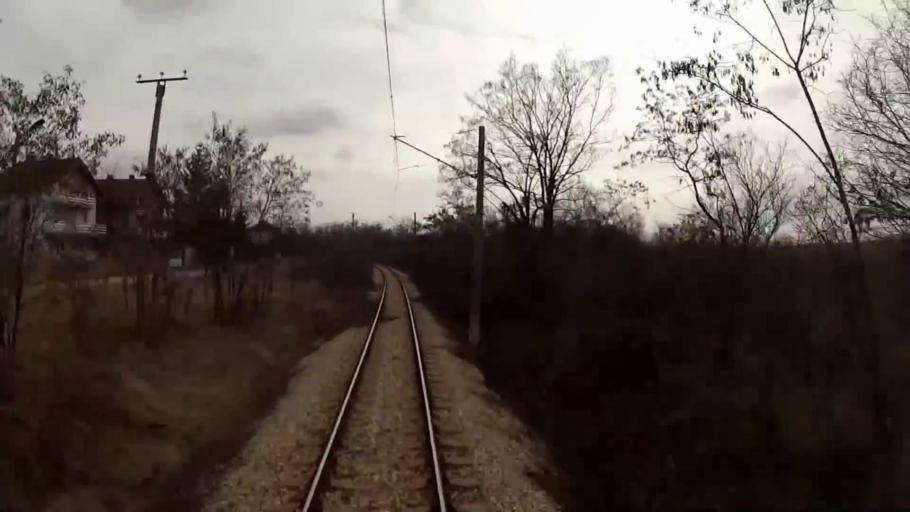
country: BG
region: Sofiya
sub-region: Obshtina Gorna Malina
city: Gorna Malina
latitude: 42.7149
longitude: 23.7395
